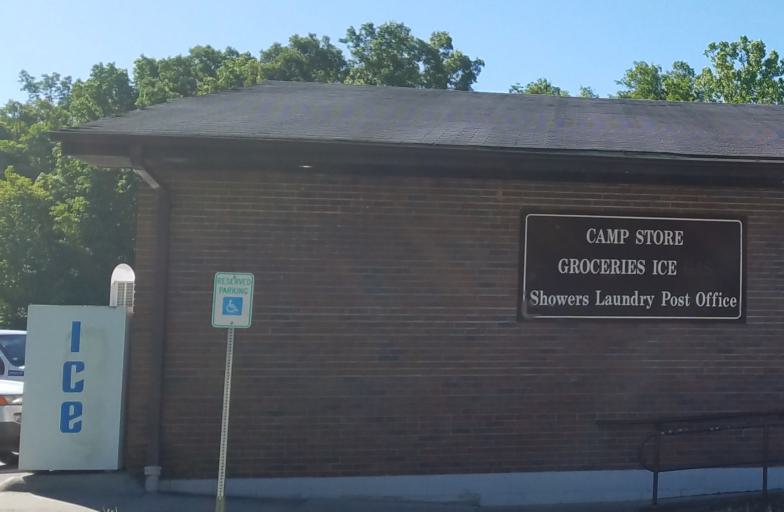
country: US
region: Kentucky
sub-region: Barren County
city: Cave City
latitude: 37.1842
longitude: -86.0981
